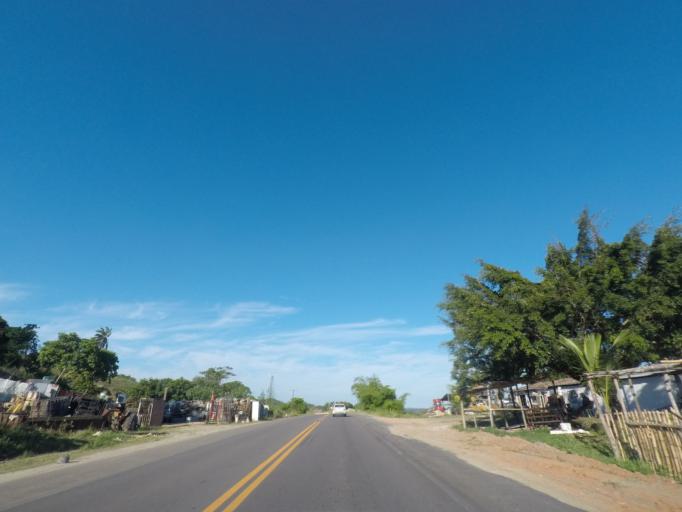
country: BR
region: Bahia
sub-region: Nazare
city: Nazare
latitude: -13.0252
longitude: -38.9888
